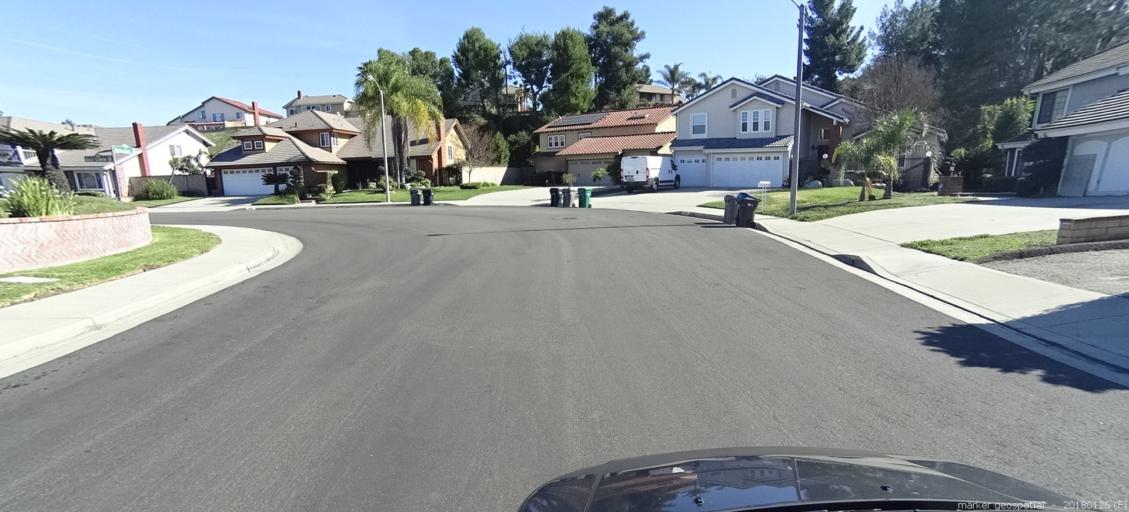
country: US
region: California
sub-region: Los Angeles County
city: Walnut
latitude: 33.9910
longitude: -117.8550
